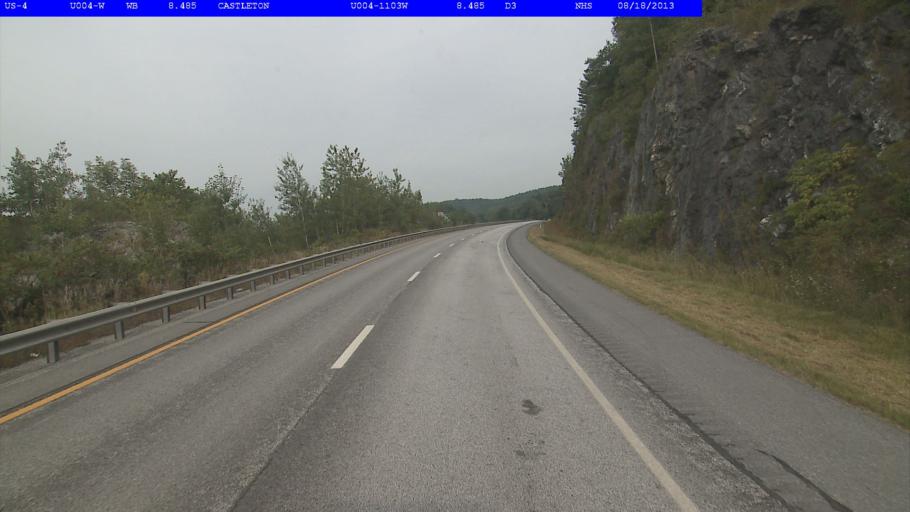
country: US
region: Vermont
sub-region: Rutland County
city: Castleton
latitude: 43.6150
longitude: -73.1506
